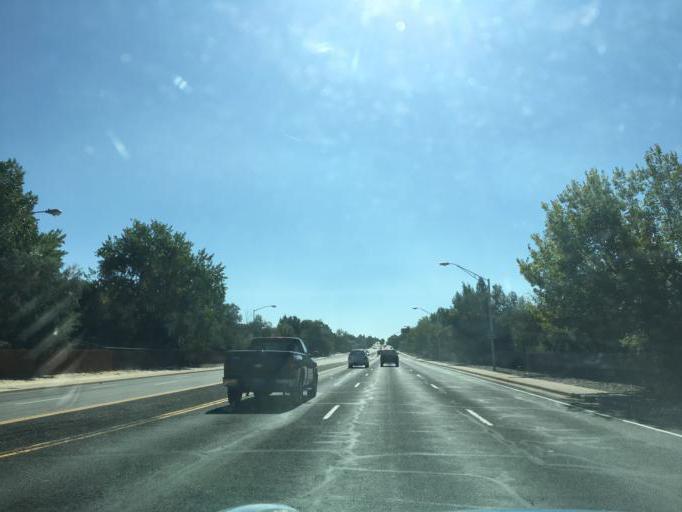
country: US
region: Colorado
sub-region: Arapahoe County
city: Dove Valley
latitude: 39.6352
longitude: -104.8178
